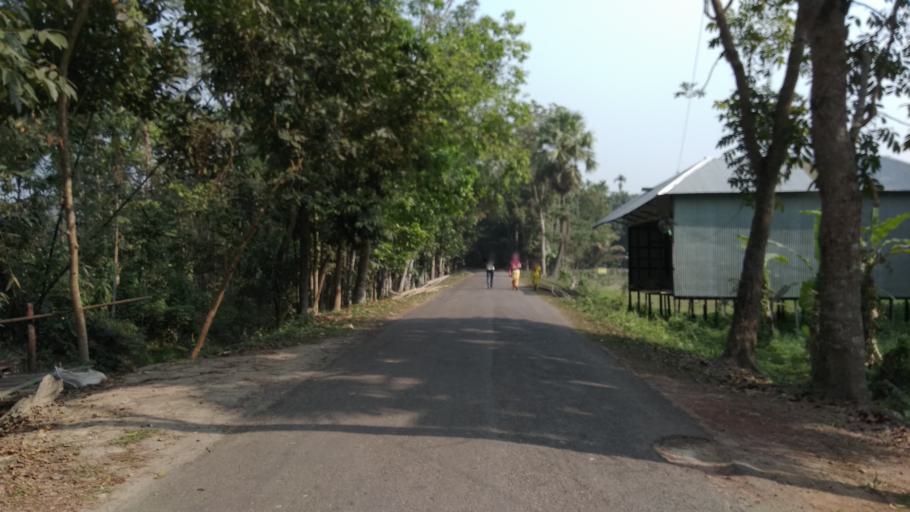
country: BD
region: Barisal
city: Mehendiganj
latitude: 22.9762
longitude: 90.4165
